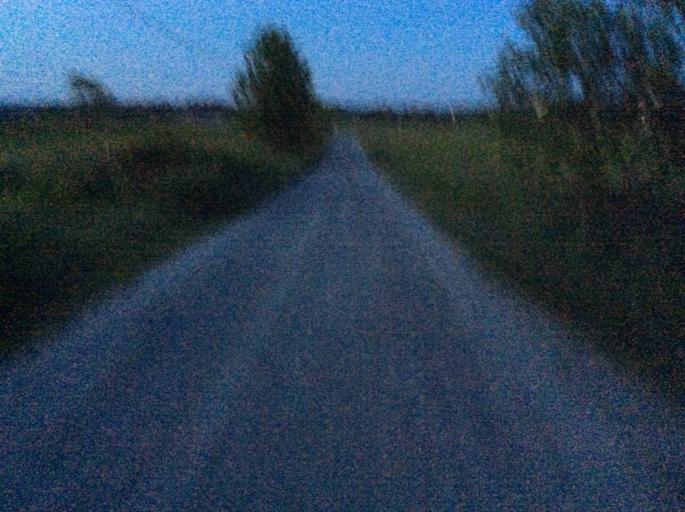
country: SE
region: Vaestra Goetaland
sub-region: Goteborg
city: Majorna
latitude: 57.7948
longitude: 11.8830
